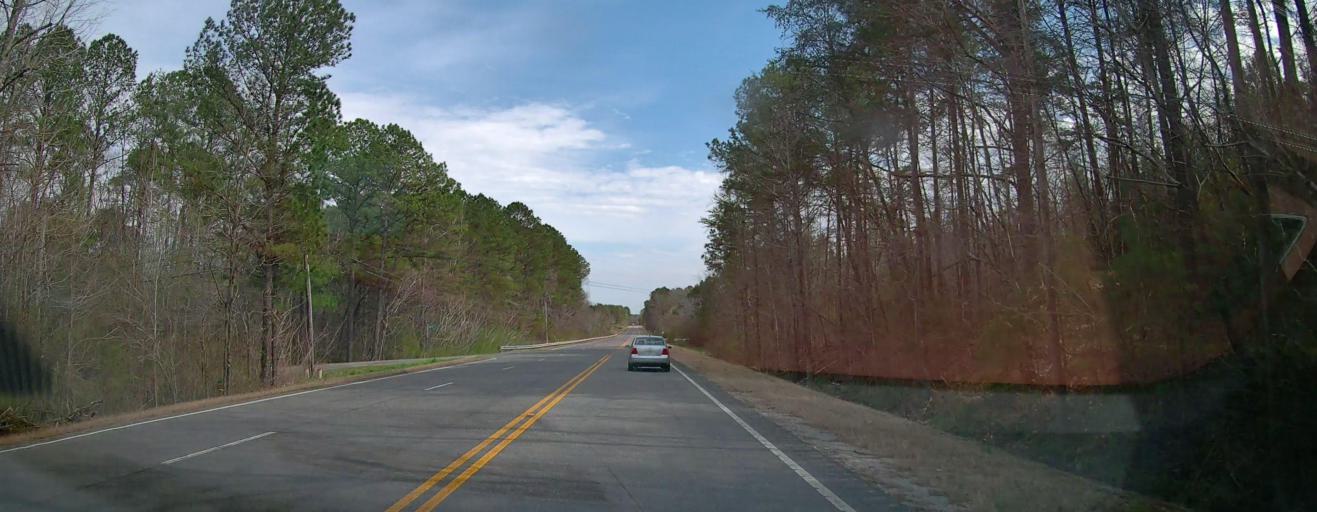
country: US
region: Alabama
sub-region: Walker County
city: Carbon Hill
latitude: 33.9109
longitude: -87.5594
